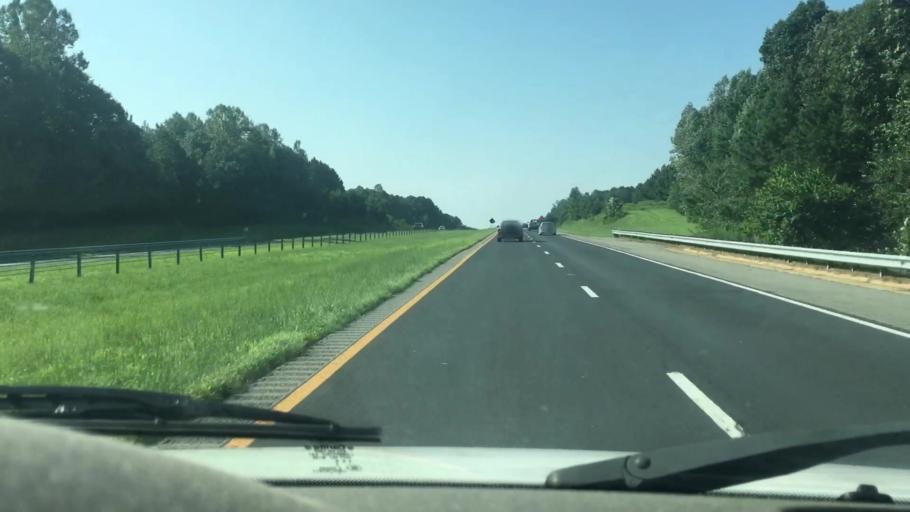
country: US
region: North Carolina
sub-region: Lincoln County
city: Lowesville
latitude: 35.4083
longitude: -80.9985
